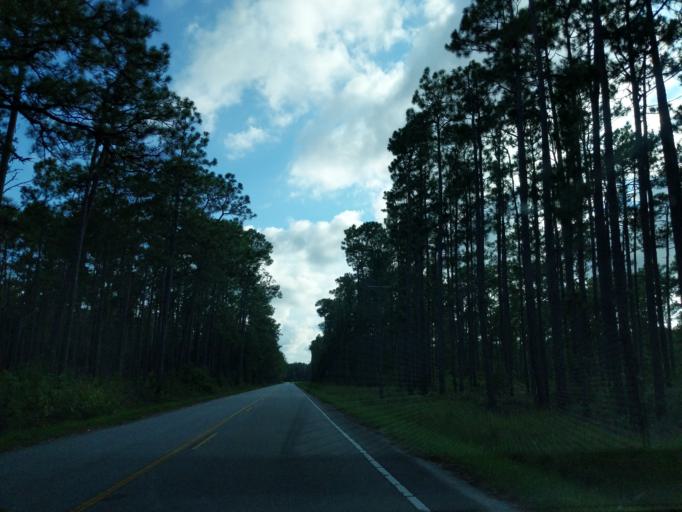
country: US
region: South Carolina
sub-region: Charleston County
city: Awendaw
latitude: 33.1321
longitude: -79.4433
